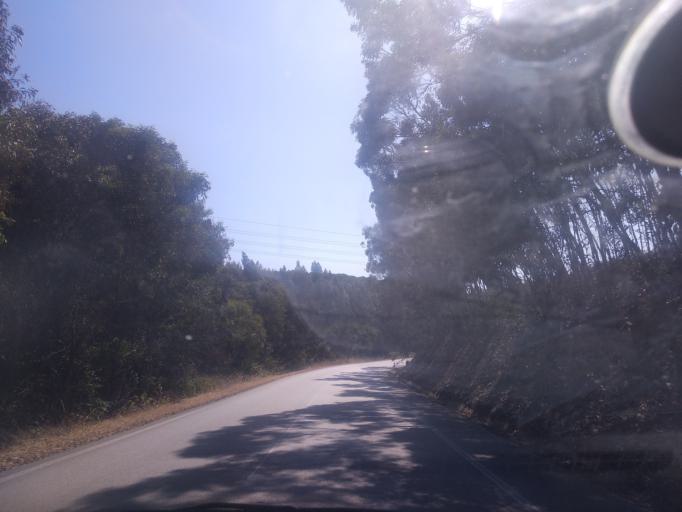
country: PT
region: Faro
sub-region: Aljezur
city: Aljezur
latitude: 37.2154
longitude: -8.7825
